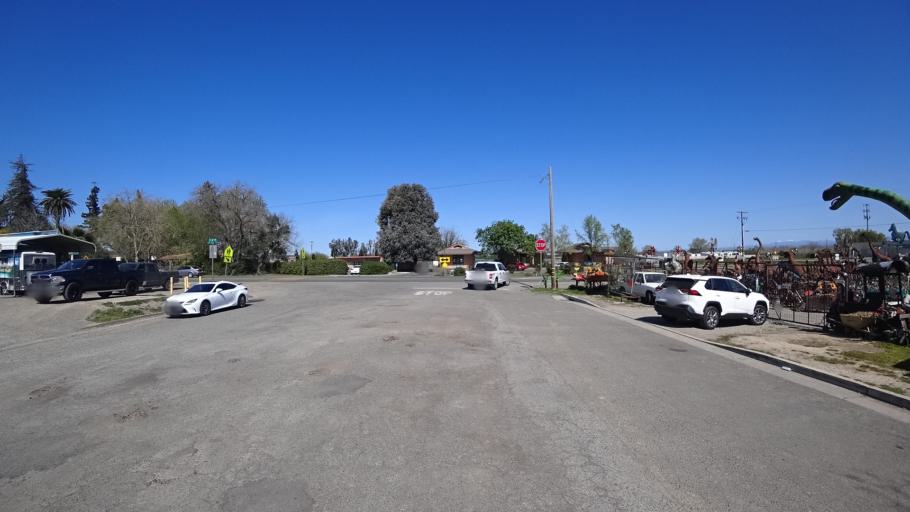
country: US
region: California
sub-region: Glenn County
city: Hamilton City
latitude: 39.7449
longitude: -122.0166
